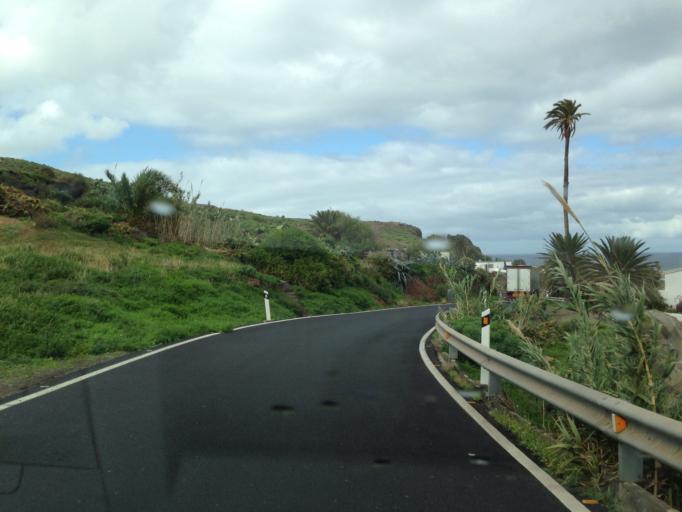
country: ES
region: Canary Islands
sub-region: Provincia de Las Palmas
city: Agaete
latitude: 28.0972
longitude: -15.7021
